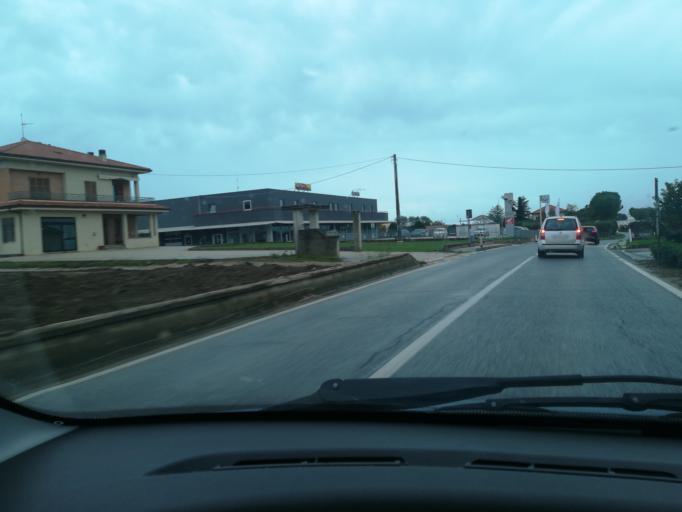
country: IT
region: The Marches
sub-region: Provincia di Macerata
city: Santa Maria Apparente
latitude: 43.2944
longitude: 13.6735
